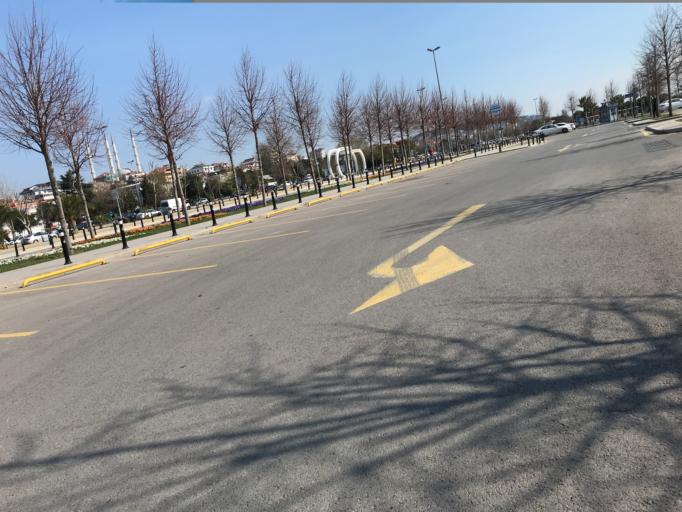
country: TR
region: Istanbul
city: Maltepe
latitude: 40.9256
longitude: 29.1225
